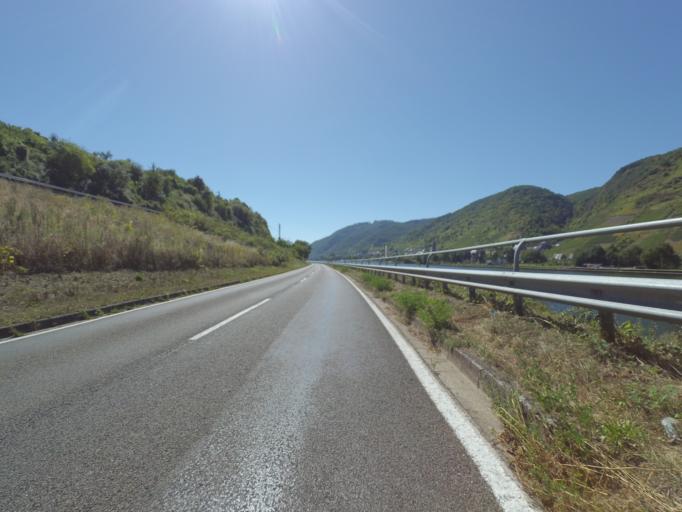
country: DE
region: Rheinland-Pfalz
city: Sankt Aldegund
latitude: 50.0855
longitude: 7.1353
